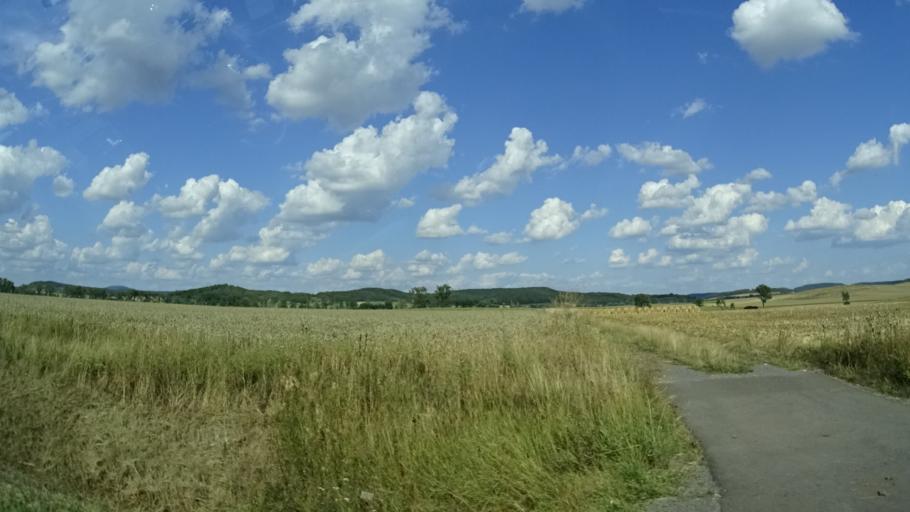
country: DE
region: Bavaria
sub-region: Regierungsbezirk Unterfranken
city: Bad Konigshofen im Grabfeld
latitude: 50.2864
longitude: 10.4879
